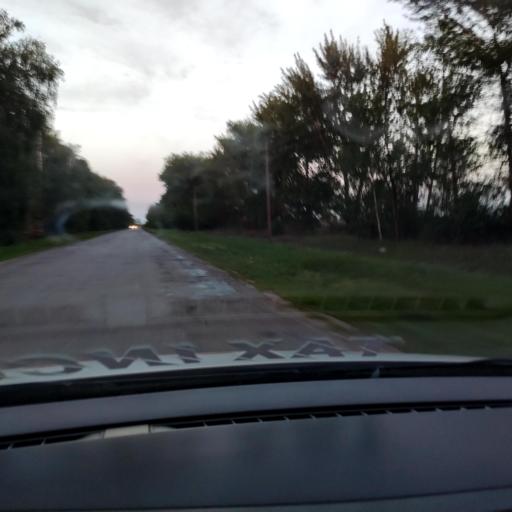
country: RU
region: Voronezj
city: Maslovka
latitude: 51.4390
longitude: 39.2901
